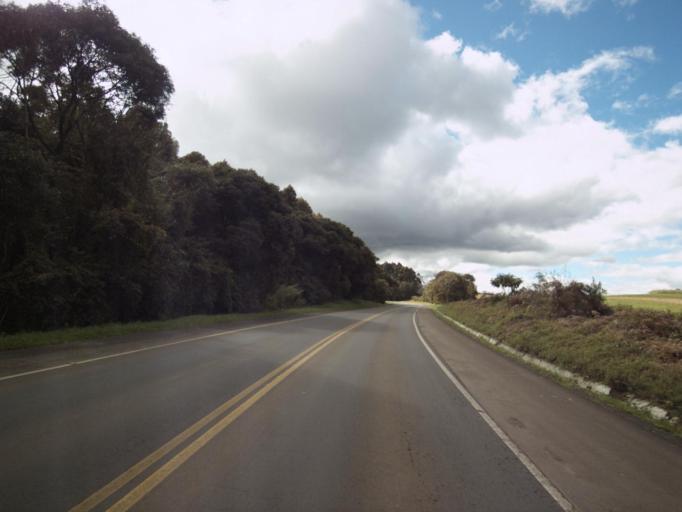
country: BR
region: Santa Catarina
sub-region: Concordia
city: Concordia
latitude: -27.2756
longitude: -51.9667
